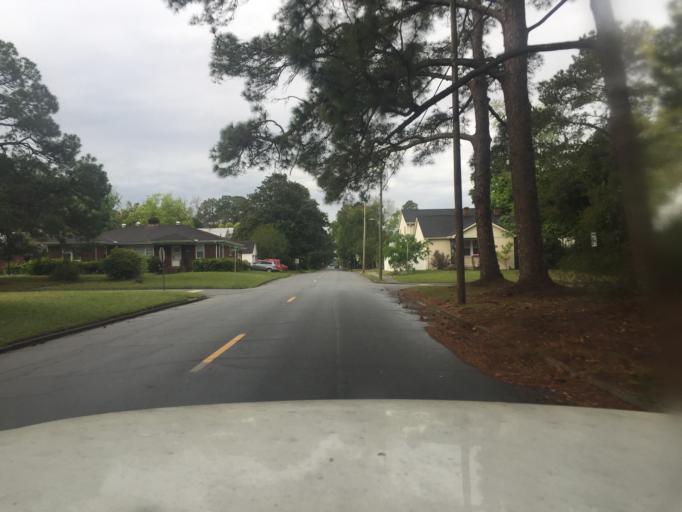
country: US
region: Georgia
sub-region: Chatham County
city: Thunderbolt
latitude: 32.0396
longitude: -81.0927
